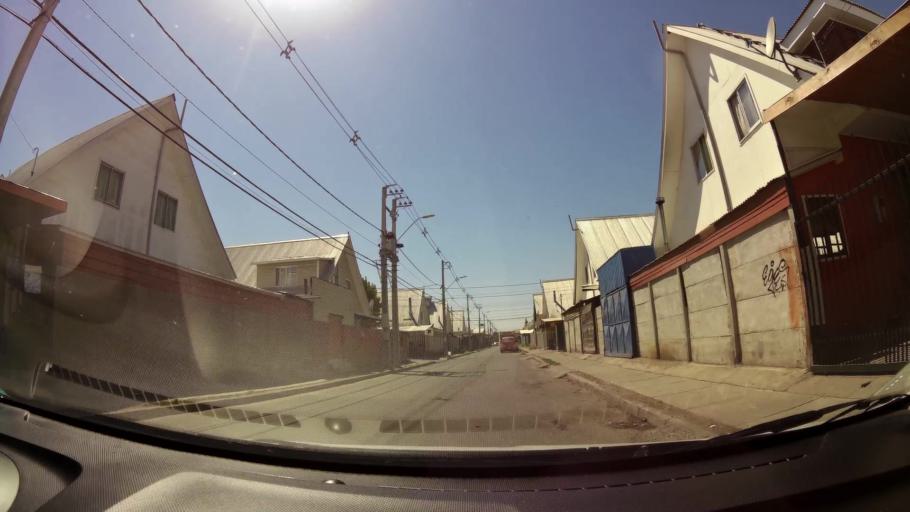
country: CL
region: Maule
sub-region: Provincia de Curico
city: Curico
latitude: -34.9653
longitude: -71.2478
